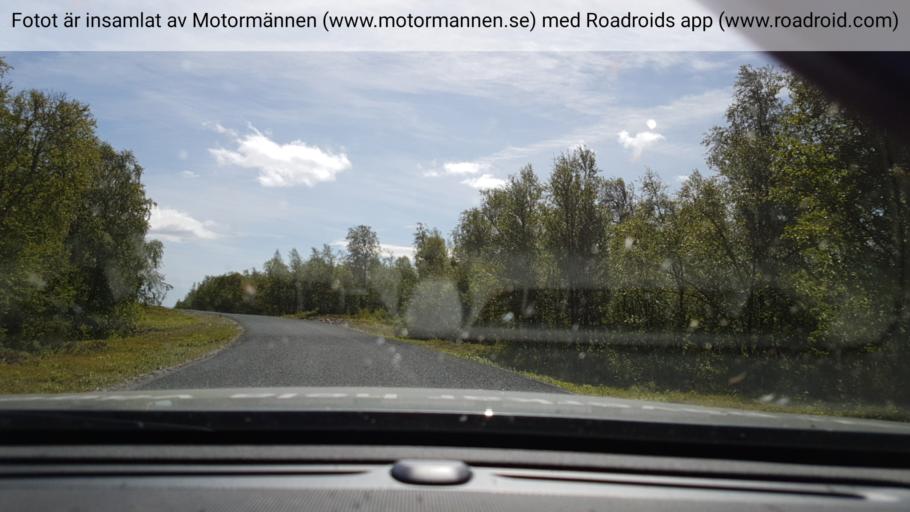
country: NO
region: Nordland
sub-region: Hattfjelldal
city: Hattfjelldal
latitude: 65.4111
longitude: 14.9338
